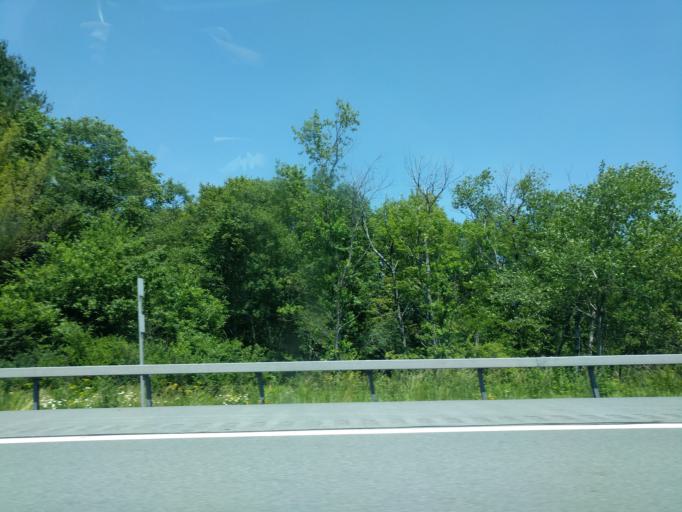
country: US
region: New York
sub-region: Sullivan County
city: Livingston Manor
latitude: 41.9247
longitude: -74.8416
